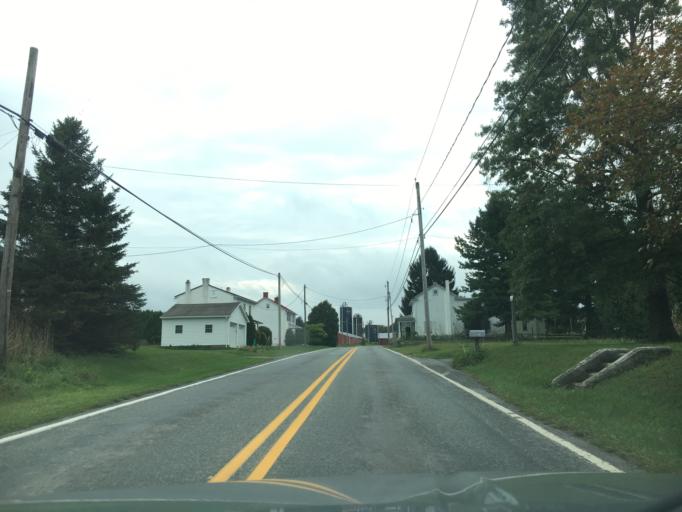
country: US
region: Pennsylvania
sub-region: Berks County
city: Topton
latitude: 40.4538
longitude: -75.7472
